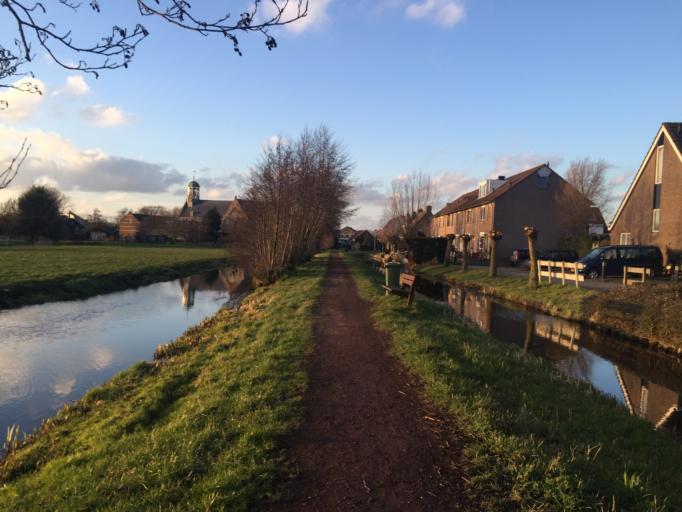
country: NL
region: Utrecht
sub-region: Gemeente Oudewater
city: Oudewater
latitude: 52.0592
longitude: 4.8209
